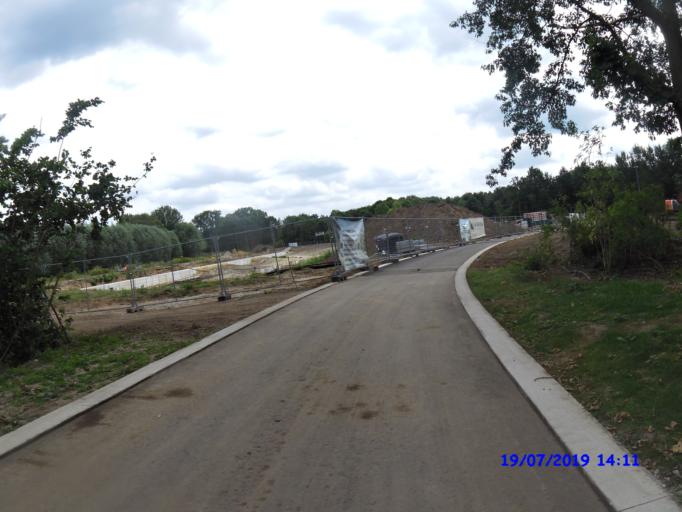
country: BE
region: Flanders
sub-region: Provincie Limburg
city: Hasselt
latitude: 50.9353
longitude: 5.3517
